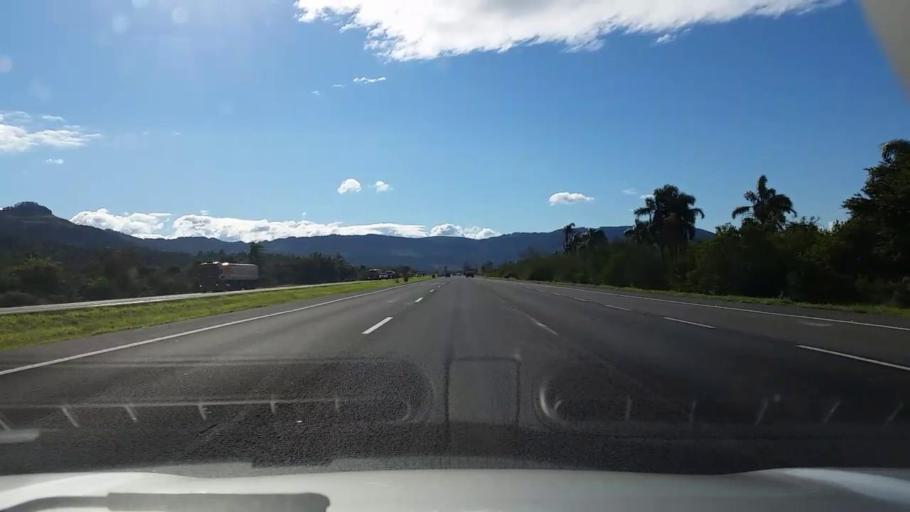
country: BR
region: Rio Grande do Sul
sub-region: Osorio
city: Osorio
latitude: -29.8837
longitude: -50.4420
